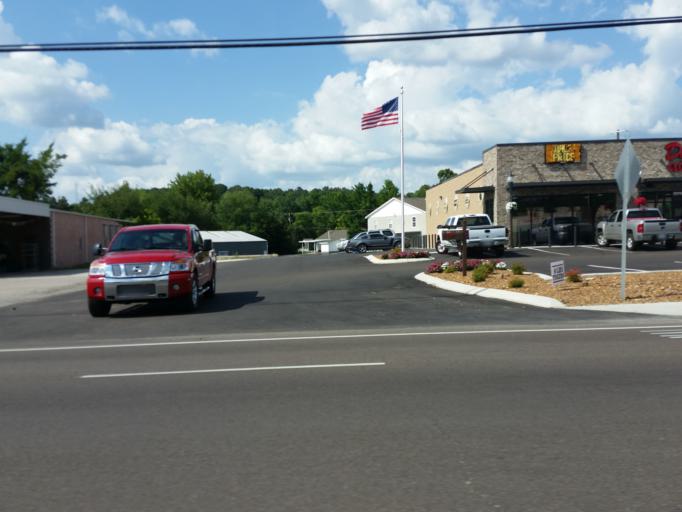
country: US
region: Tennessee
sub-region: Henderson County
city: Lexington
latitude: 35.6570
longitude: -88.4099
